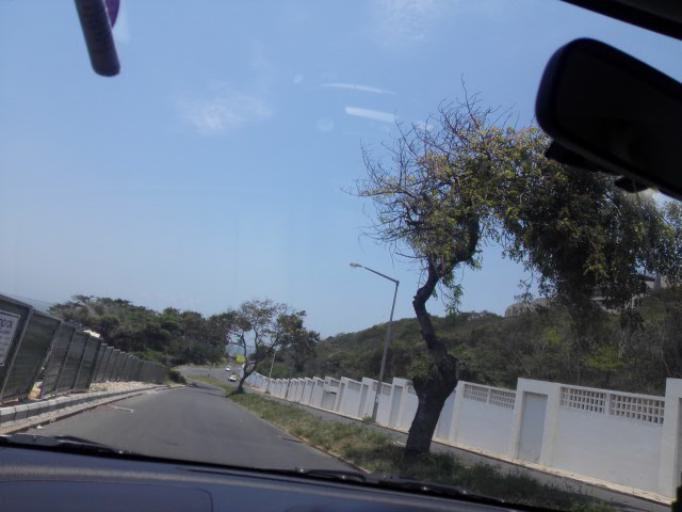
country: MZ
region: Maputo City
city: Maputo
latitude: -25.9636
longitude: 32.6023
